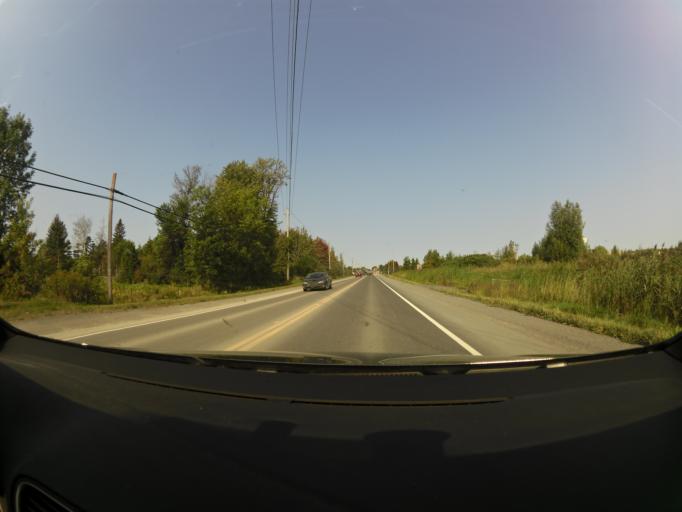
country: CA
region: Ontario
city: Bells Corners
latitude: 45.2895
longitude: -75.9675
